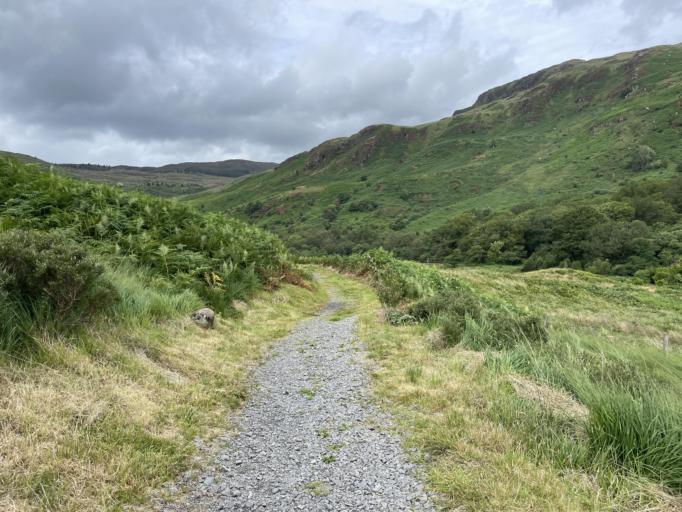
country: GB
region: Scotland
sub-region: Dumfries and Galloway
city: Newton Stewart
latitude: 55.0898
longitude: -4.4666
